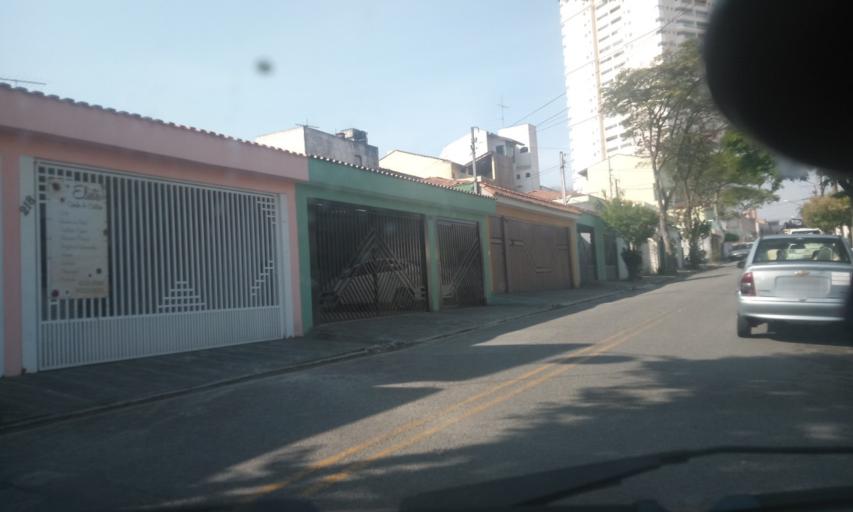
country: BR
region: Sao Paulo
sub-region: Sao Bernardo Do Campo
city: Sao Bernardo do Campo
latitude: -23.7142
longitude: -46.5566
